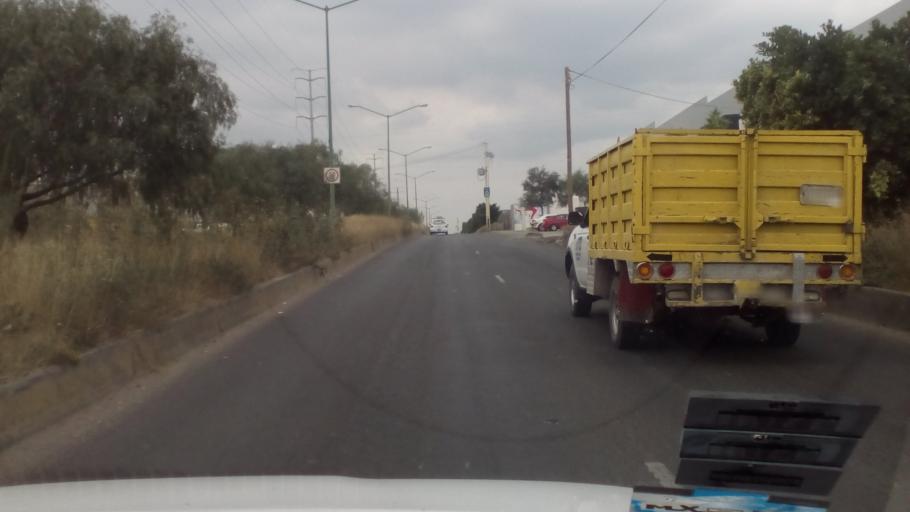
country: MX
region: Guanajuato
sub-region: Leon
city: La Ermita
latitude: 21.1542
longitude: -101.7303
